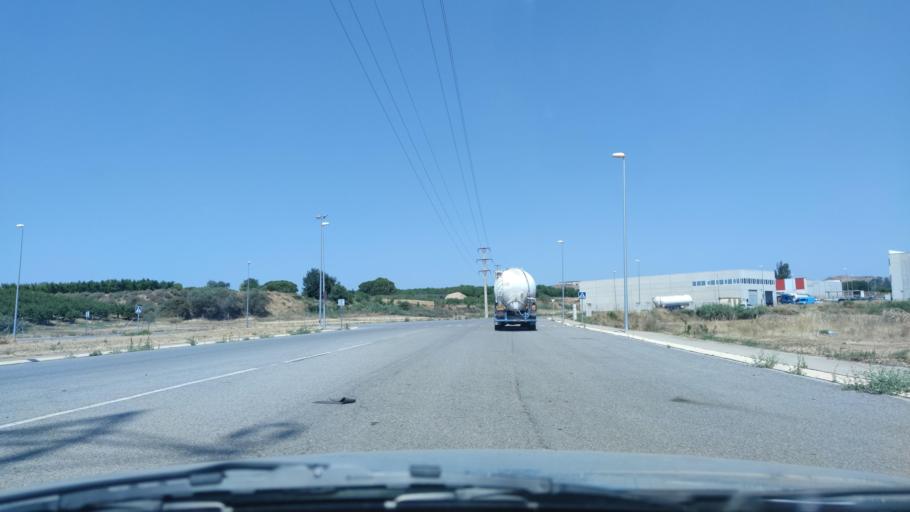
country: ES
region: Catalonia
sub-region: Provincia de Lleida
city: Torrefarrera
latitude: 41.6660
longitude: 0.5987
